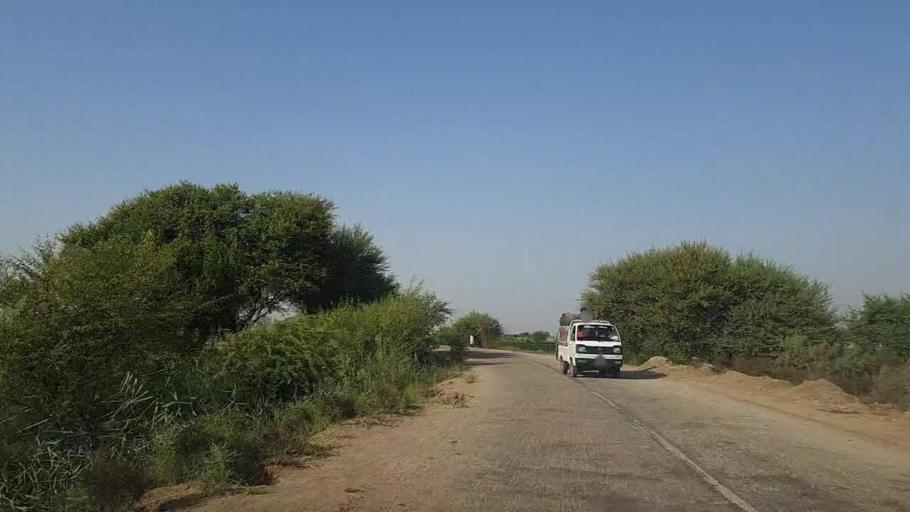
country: PK
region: Sindh
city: Mirpur Batoro
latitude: 24.5766
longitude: 68.3949
